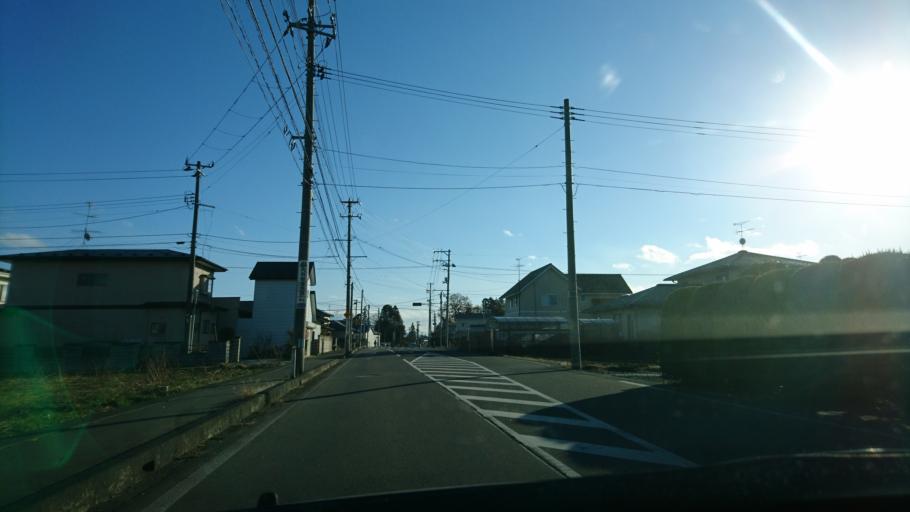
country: JP
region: Iwate
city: Mizusawa
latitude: 39.1199
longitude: 141.1557
